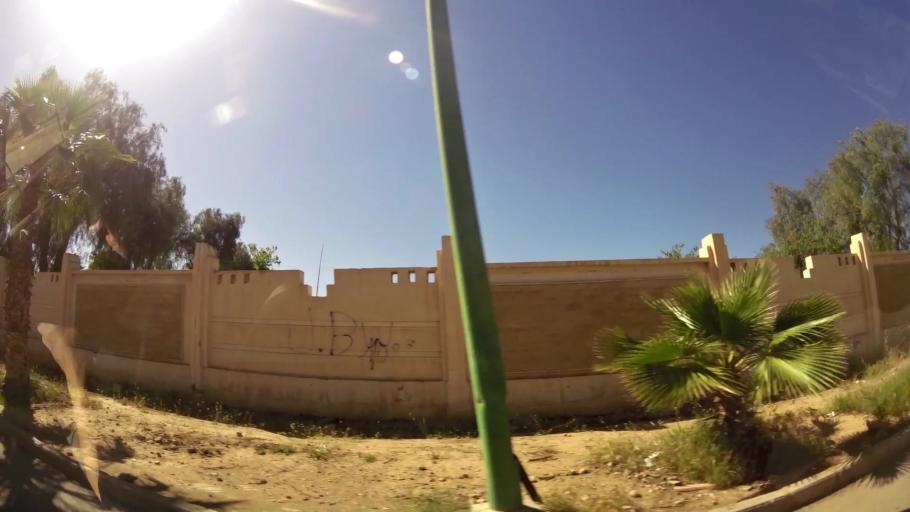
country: MA
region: Oriental
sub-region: Oujda-Angad
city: Oujda
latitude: 34.7174
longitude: -1.9183
